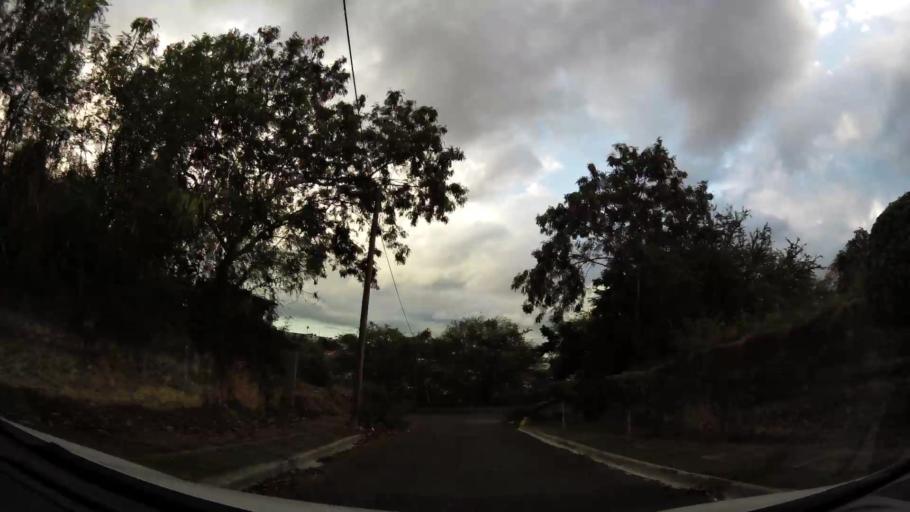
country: DO
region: Nacional
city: Santo Domingo
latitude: 18.4994
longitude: -69.9686
